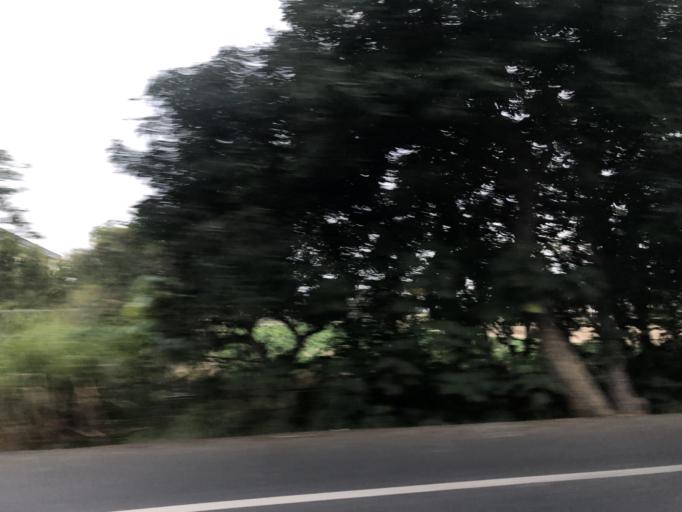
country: TW
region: Taiwan
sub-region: Tainan
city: Tainan
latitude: 23.0229
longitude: 120.3034
